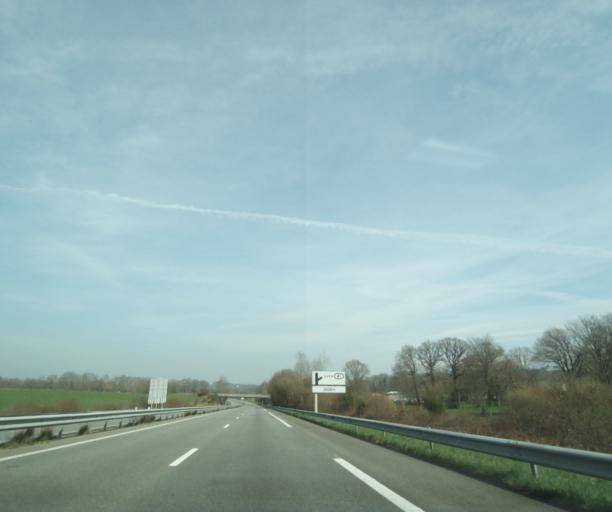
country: FR
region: Limousin
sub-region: Departement de la Haute-Vienne
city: Saint-Germain-les-Belles
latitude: 45.6086
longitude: 1.4482
